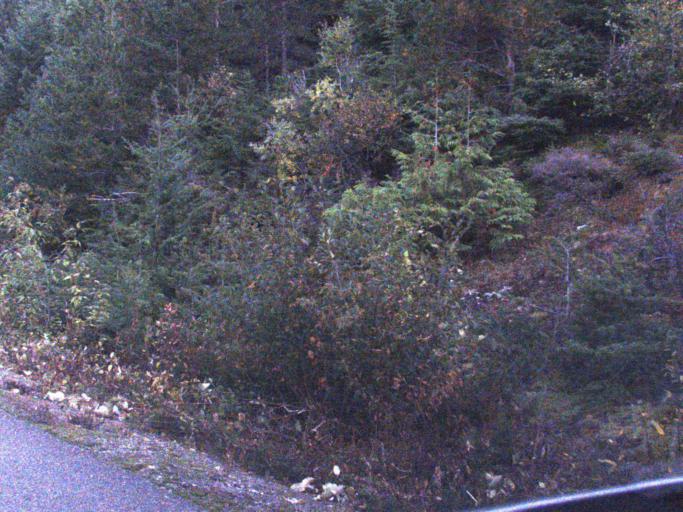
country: US
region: Washington
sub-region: Snohomish County
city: Darrington
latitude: 48.7228
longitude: -121.0202
